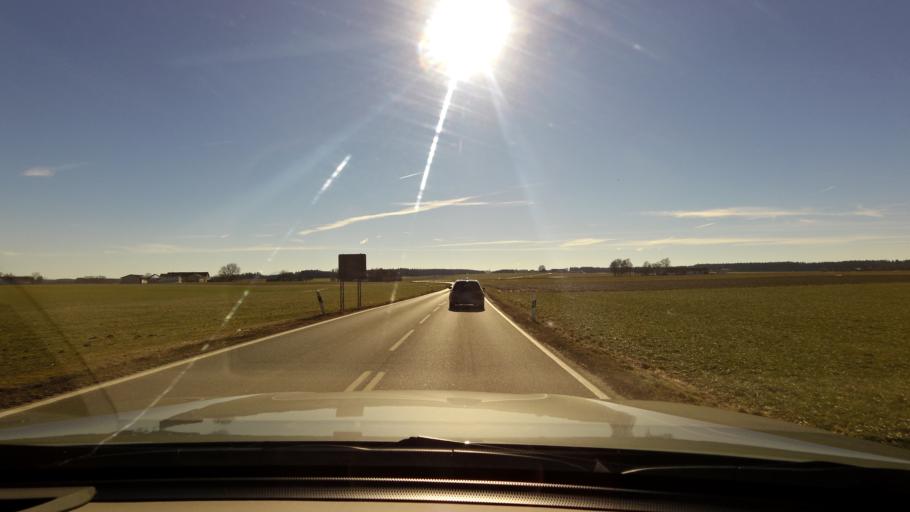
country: DE
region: Bavaria
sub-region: Upper Bavaria
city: Taufkirchen
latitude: 48.1743
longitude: 12.4602
